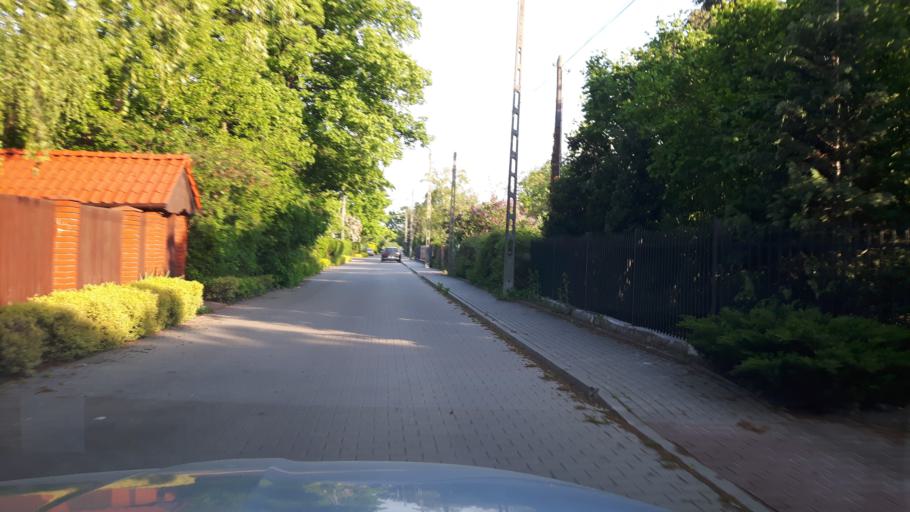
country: PL
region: Masovian Voivodeship
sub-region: Warszawa
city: Rembertow
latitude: 52.2672
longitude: 21.1519
